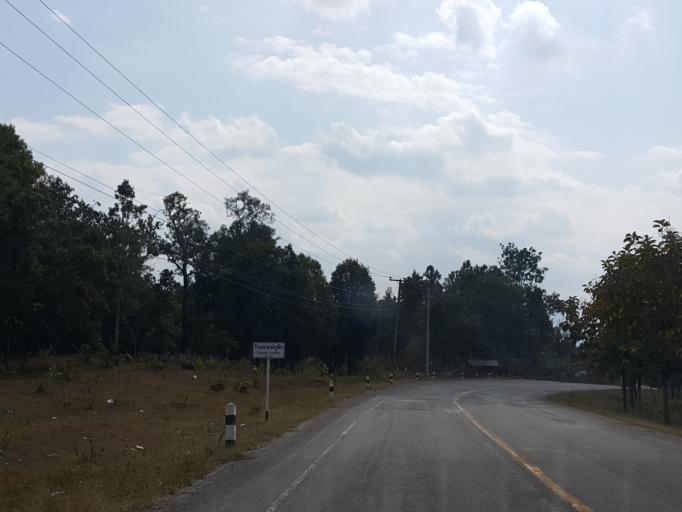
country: TH
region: Chiang Mai
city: Om Koi
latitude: 17.8378
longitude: 98.3728
